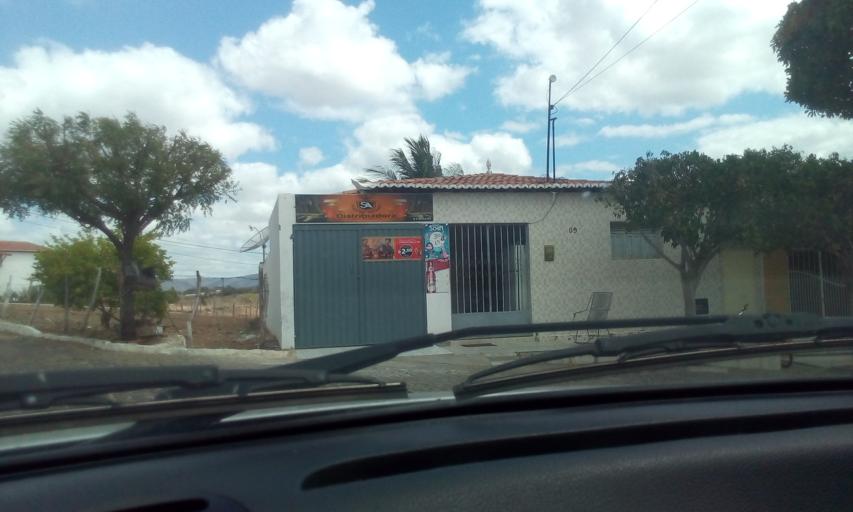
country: BR
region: Rio Grande do Norte
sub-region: Currais Novos
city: Currais Novos
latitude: -6.2147
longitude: -36.6806
